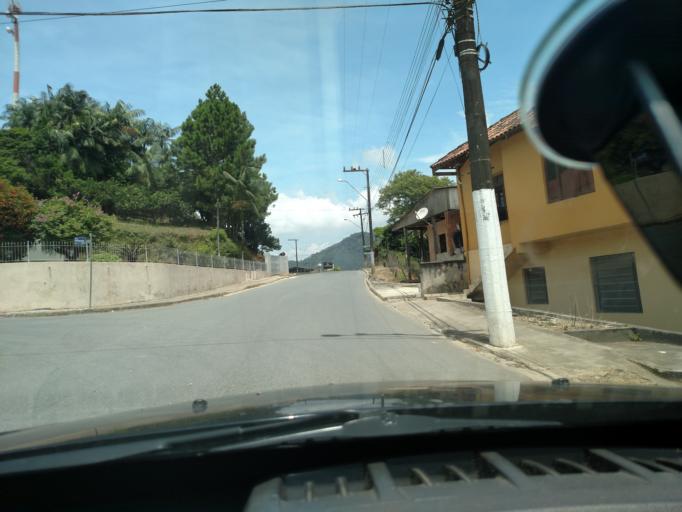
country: BR
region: Santa Catarina
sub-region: Gaspar
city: Gaspar
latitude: -26.9030
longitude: -48.8254
